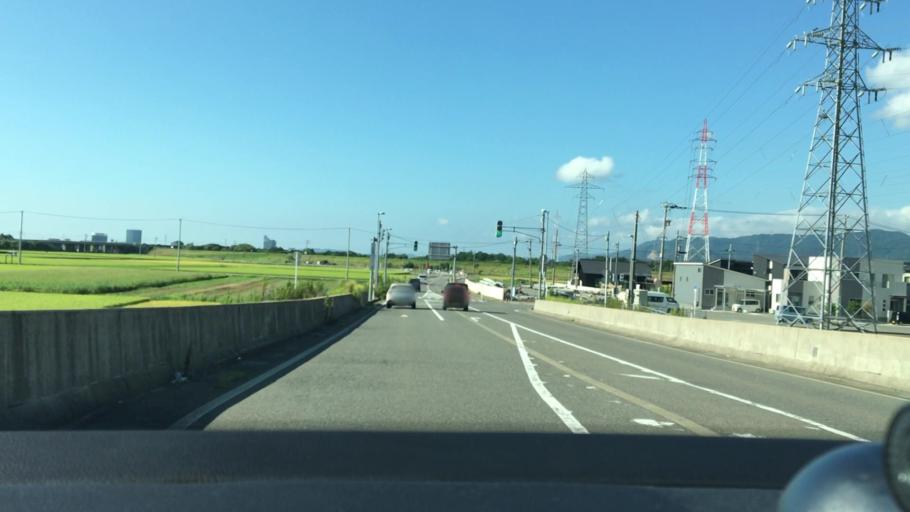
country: JP
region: Fukui
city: Maruoka
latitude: 36.0924
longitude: 136.2819
